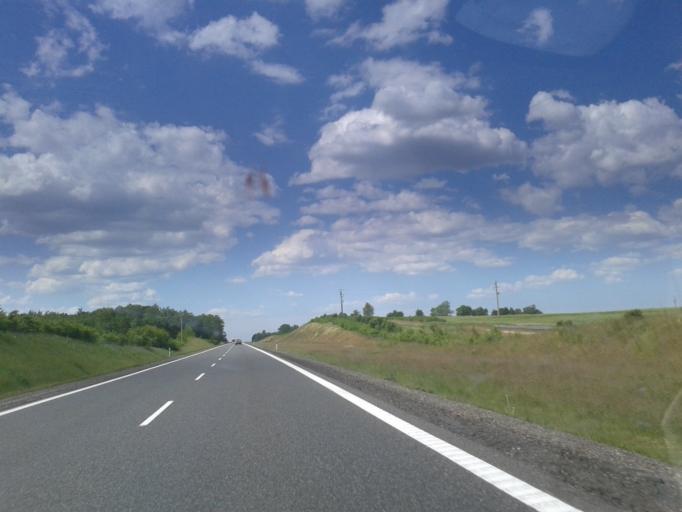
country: PL
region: Pomeranian Voivodeship
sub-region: Powiat chojnicki
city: Chojnice
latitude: 53.6833
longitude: 17.5254
